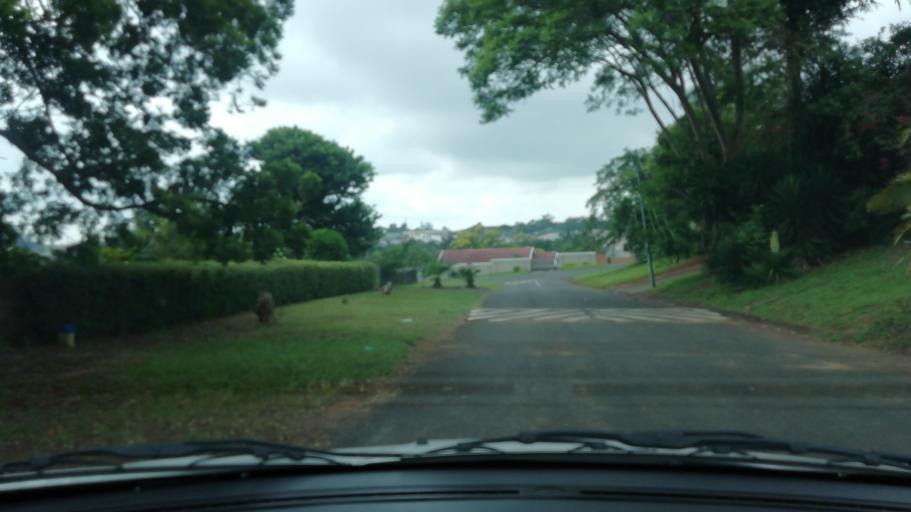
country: ZA
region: KwaZulu-Natal
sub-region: uThungulu District Municipality
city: Empangeni
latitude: -28.7650
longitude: 31.9016
